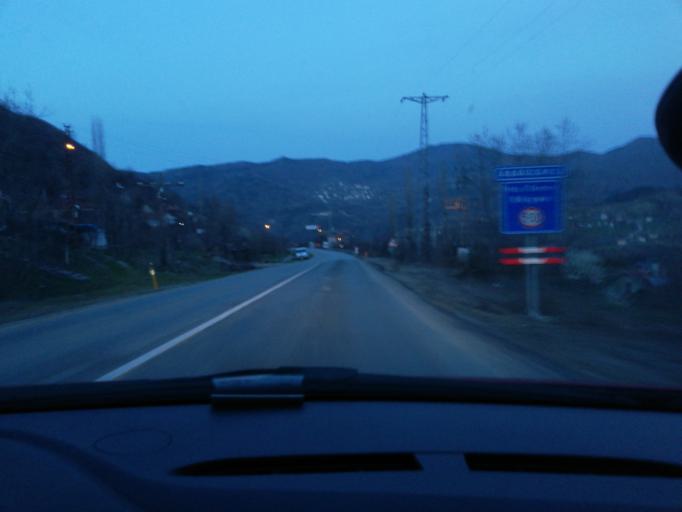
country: TR
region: Kastamonu
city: Inebolu
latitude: 41.9373
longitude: 33.7548
